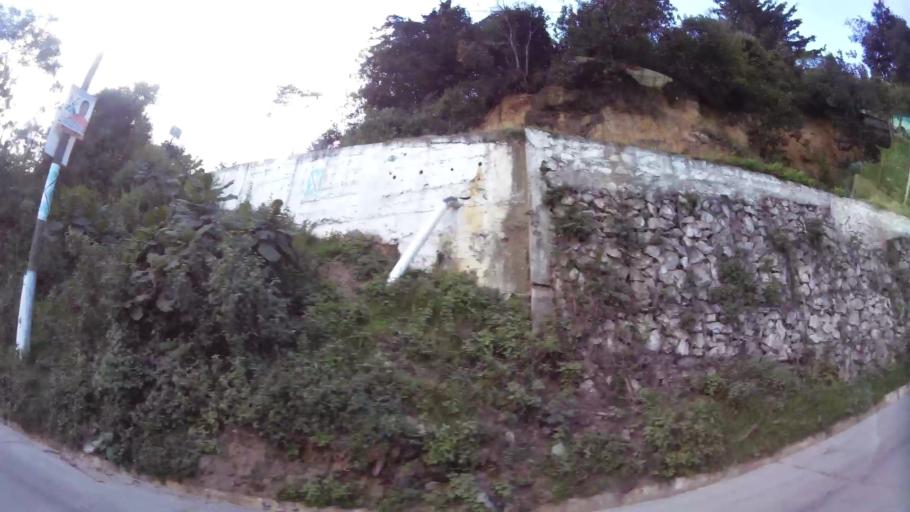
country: GT
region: Quiche
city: Chichicastenango
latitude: 14.9422
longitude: -91.1155
